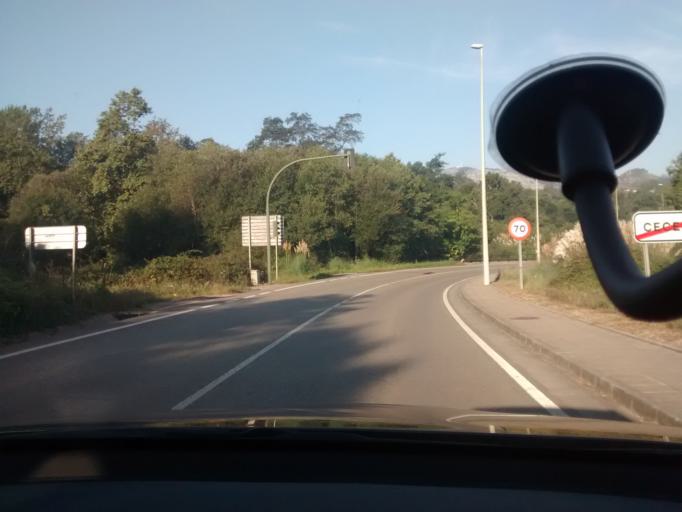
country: ES
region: Cantabria
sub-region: Provincia de Cantabria
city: Lierganes
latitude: 43.3783
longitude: -3.7242
